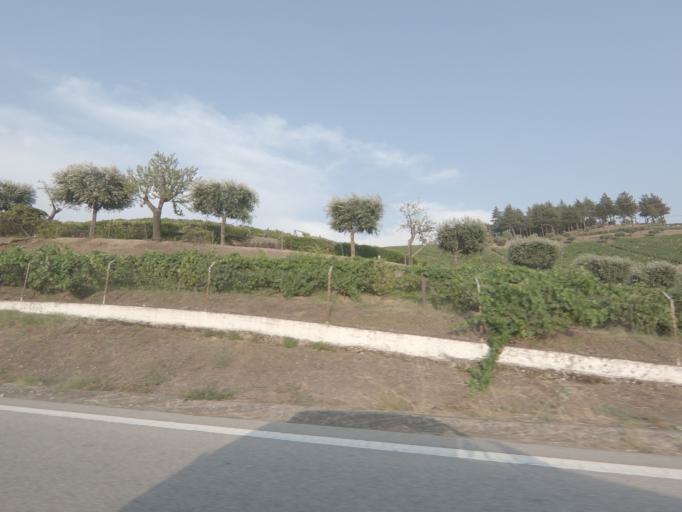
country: PT
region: Viseu
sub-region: Armamar
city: Armamar
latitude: 41.1472
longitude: -7.6865
